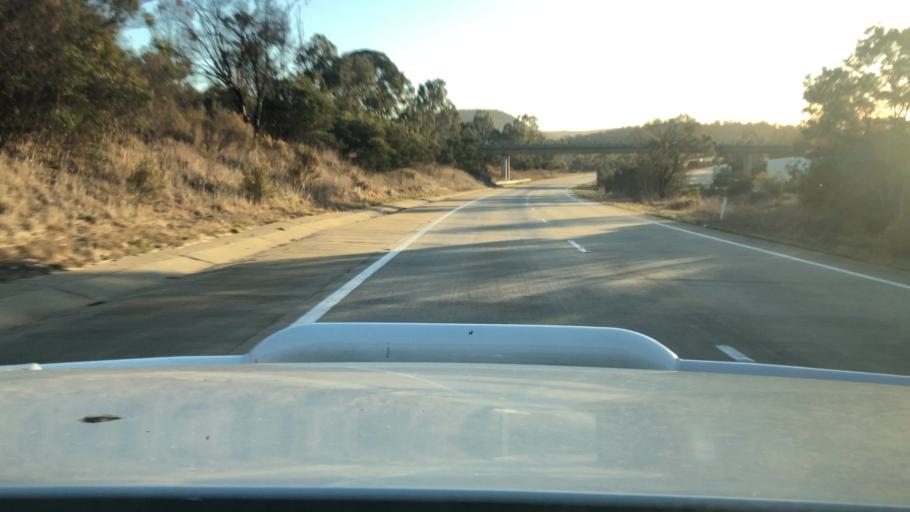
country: AU
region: New South Wales
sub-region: Goulburn Mulwaree
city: Goulburn
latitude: -34.7437
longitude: 149.7706
